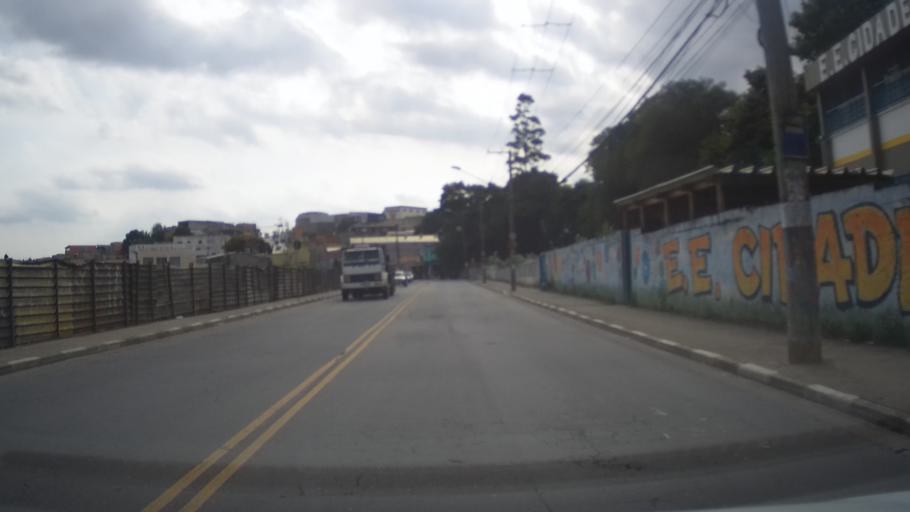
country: BR
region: Sao Paulo
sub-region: Guarulhos
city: Guarulhos
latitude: -23.4143
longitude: -46.4508
